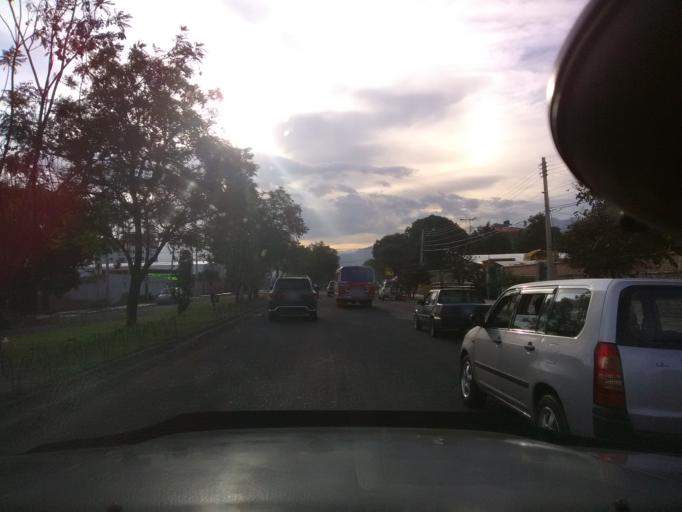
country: BO
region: Cochabamba
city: Cochabamba
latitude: -17.3925
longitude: -66.1777
